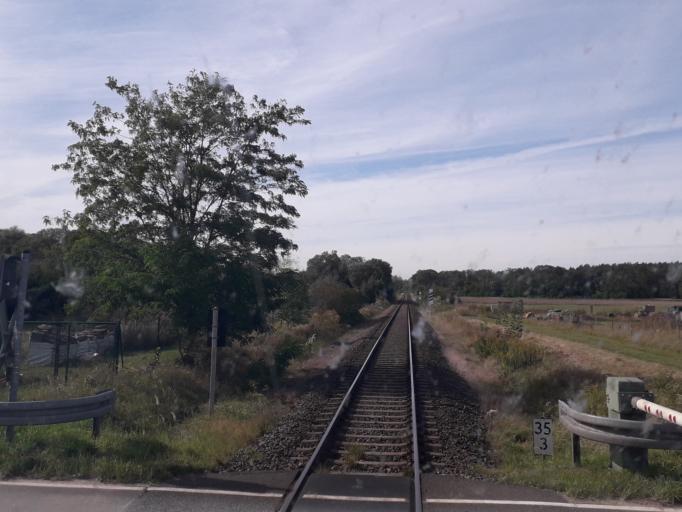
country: DE
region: Brandenburg
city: Kremmen
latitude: 52.7438
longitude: 13.0624
